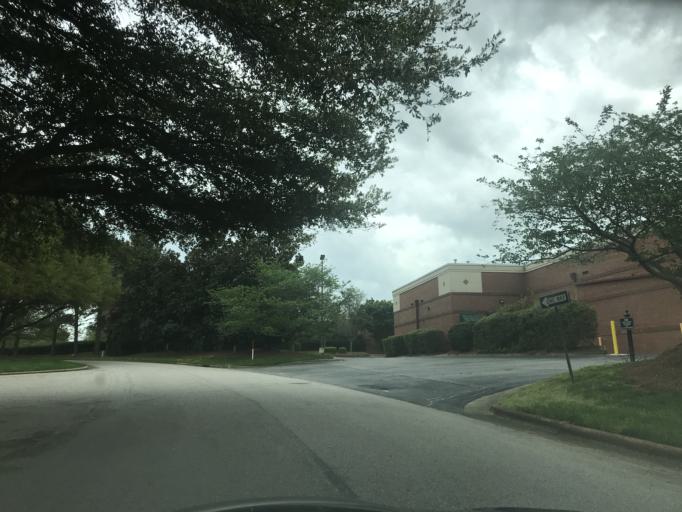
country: US
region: North Carolina
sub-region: Wake County
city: Raleigh
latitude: 35.8574
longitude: -78.5794
